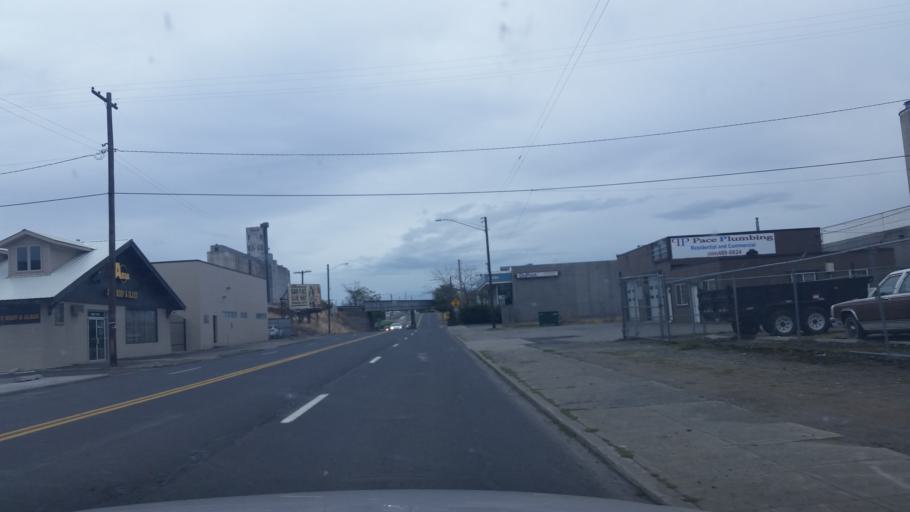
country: US
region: Washington
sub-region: Spokane County
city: Spokane
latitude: 47.6618
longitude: -117.3839
